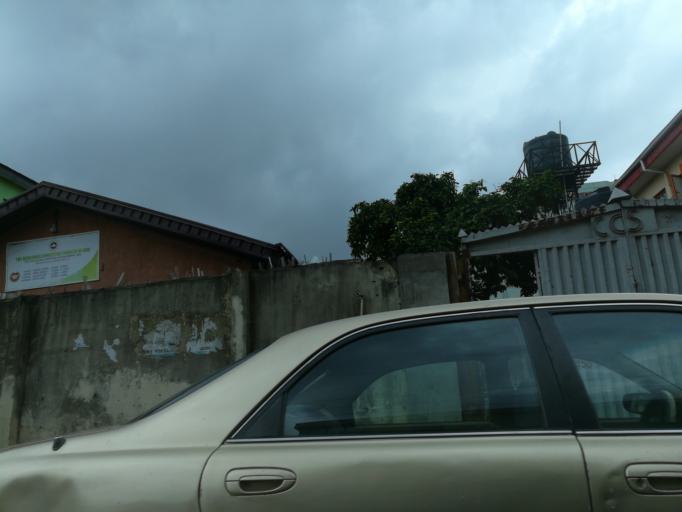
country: NG
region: Lagos
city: Agege
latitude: 6.6031
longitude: 3.3057
